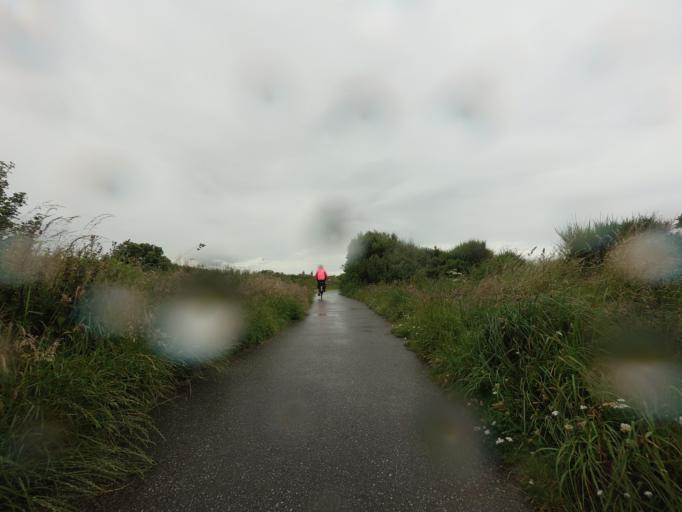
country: GB
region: Scotland
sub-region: Moray
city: Findochty
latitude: 57.6871
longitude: -2.9259
